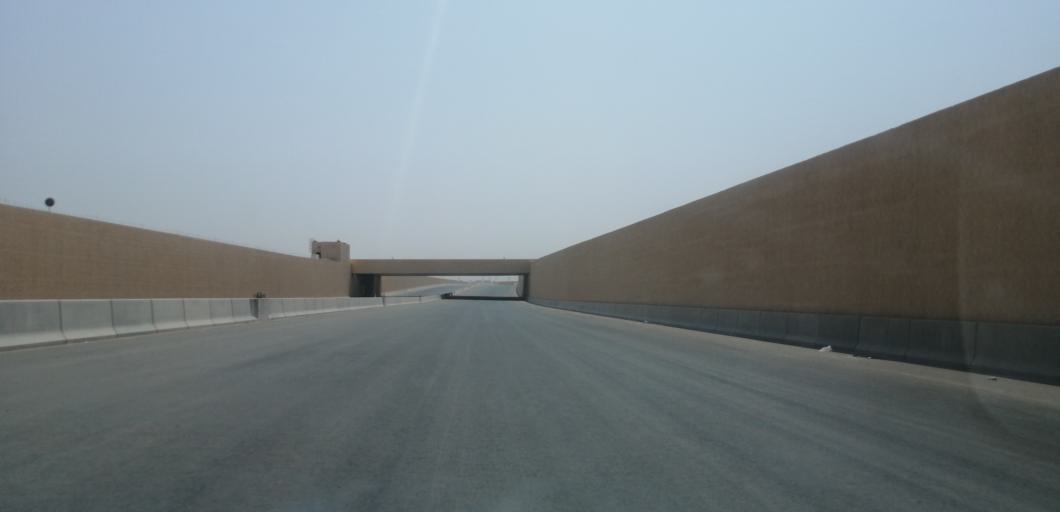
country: KW
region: Muhafazat al Jahra'
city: Al Jahra'
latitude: 29.4525
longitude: 47.5949
